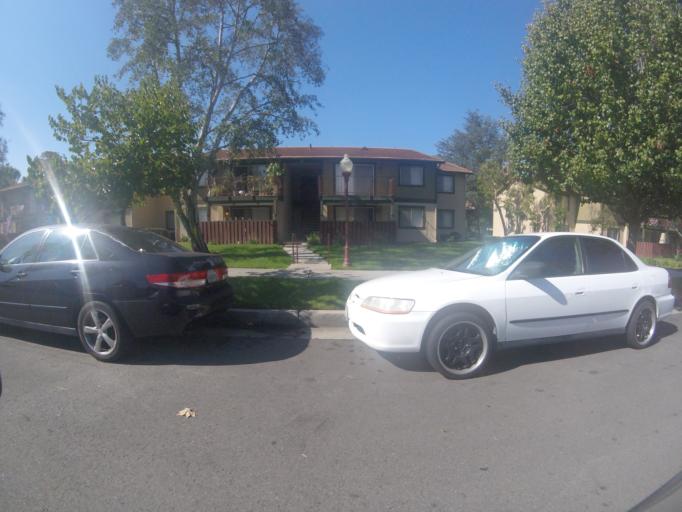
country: US
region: California
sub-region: San Bernardino County
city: Redlands
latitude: 34.0548
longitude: -117.1956
